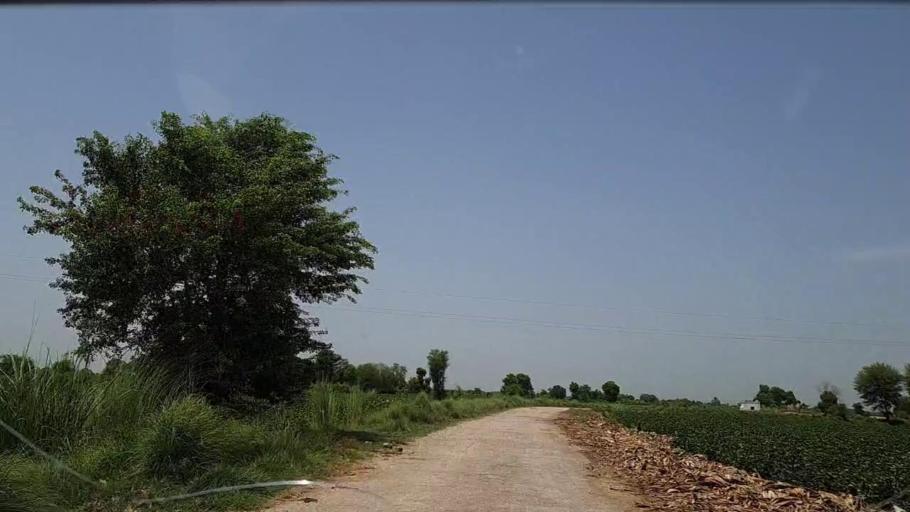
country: PK
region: Sindh
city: Tharu Shah
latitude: 26.9430
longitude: 68.0413
